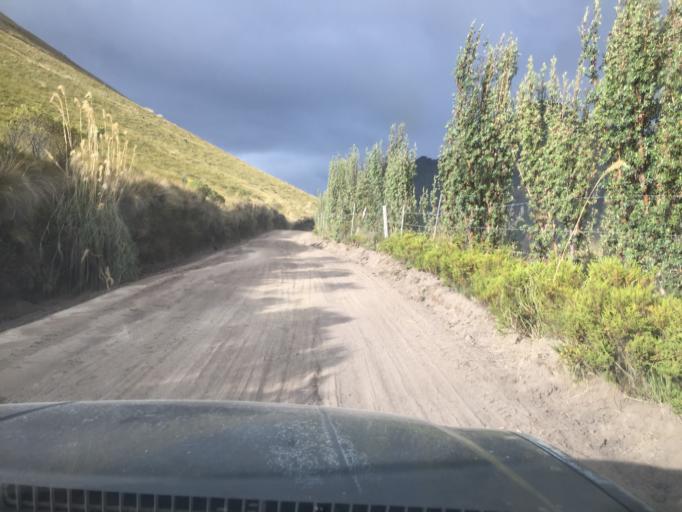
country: EC
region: Imbabura
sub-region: Canton Otavalo
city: Otavalo
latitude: 0.1142
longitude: -78.2763
